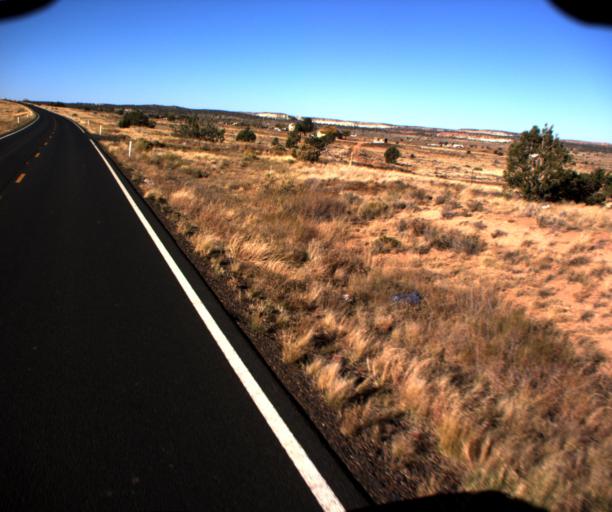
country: US
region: Arizona
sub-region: Apache County
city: Ganado
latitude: 35.7811
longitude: -109.7235
